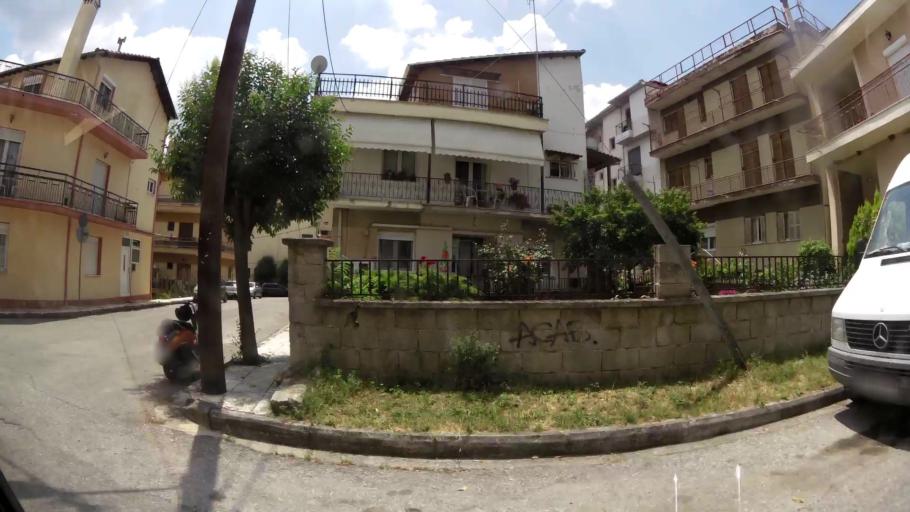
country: GR
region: West Macedonia
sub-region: Nomos Kozanis
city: Kozani
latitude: 40.2955
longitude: 21.7831
